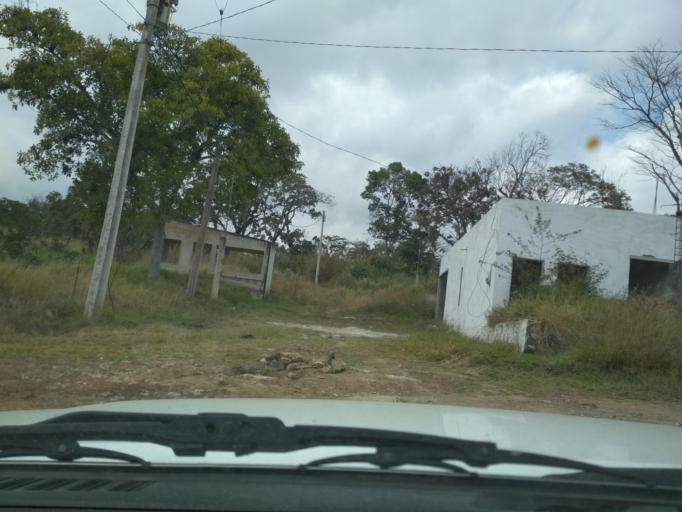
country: MX
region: Veracruz
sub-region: Coatepec
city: Bella Esperanza
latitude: 19.4554
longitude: -96.8630
